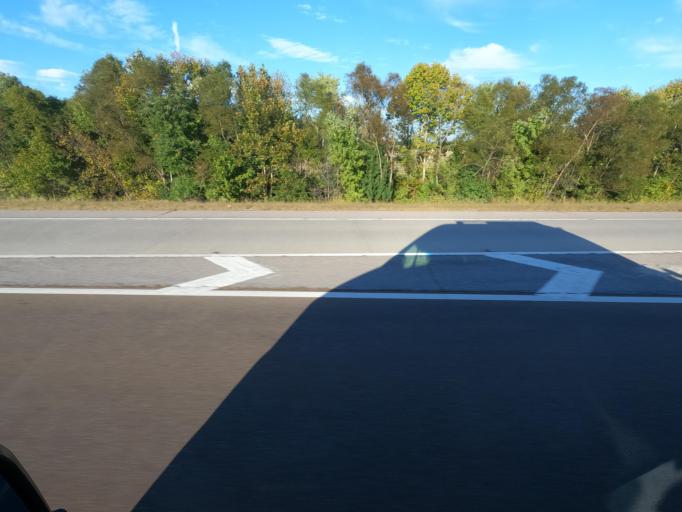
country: US
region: Tennessee
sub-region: Shelby County
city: Arlington
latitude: 35.2922
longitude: -89.6898
